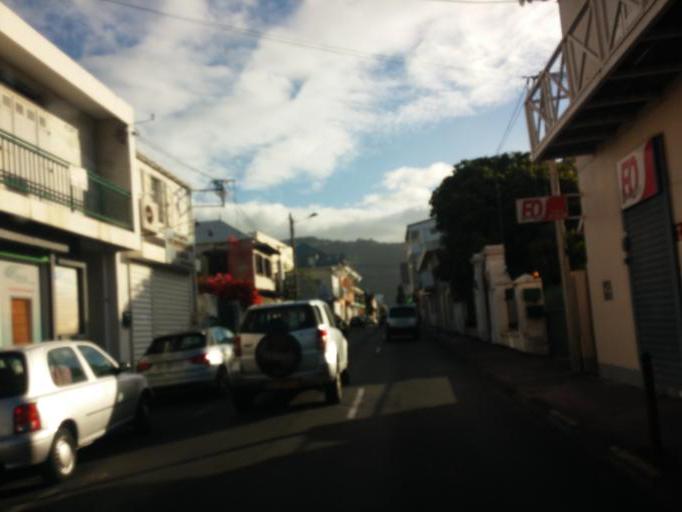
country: RE
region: Reunion
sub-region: Reunion
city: Saint-Denis
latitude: -20.8755
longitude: 55.4528
